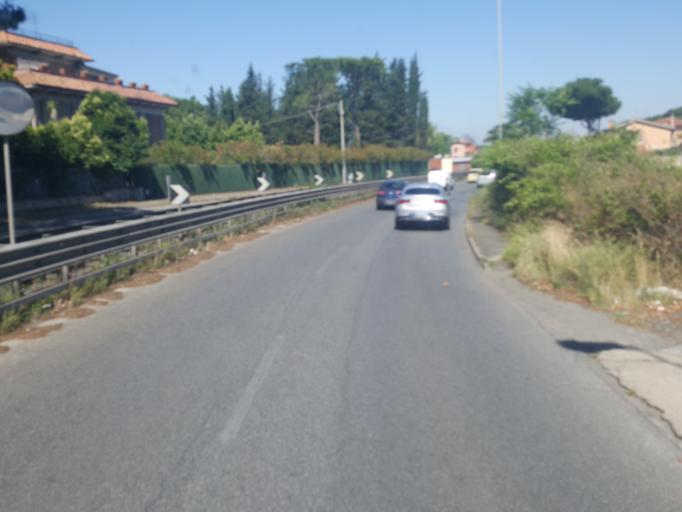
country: IT
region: Latium
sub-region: Citta metropolitana di Roma Capitale
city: Frascati
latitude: 41.8238
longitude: 12.6326
